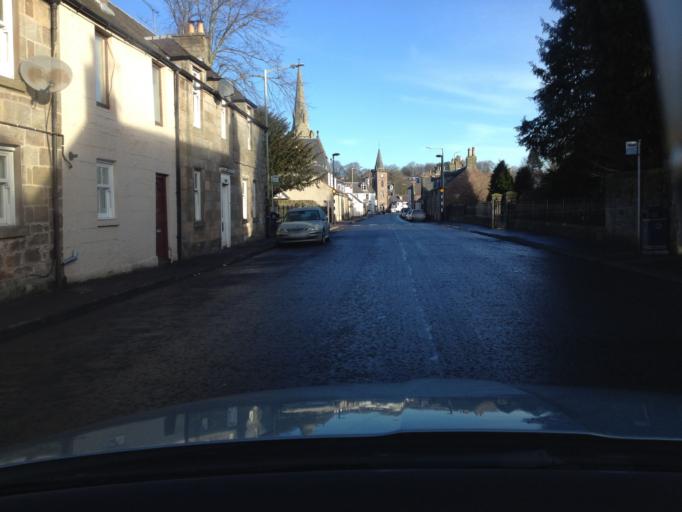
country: GB
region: Scotland
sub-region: Perth and Kinross
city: Milnathort
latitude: 56.2249
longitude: -3.4217
